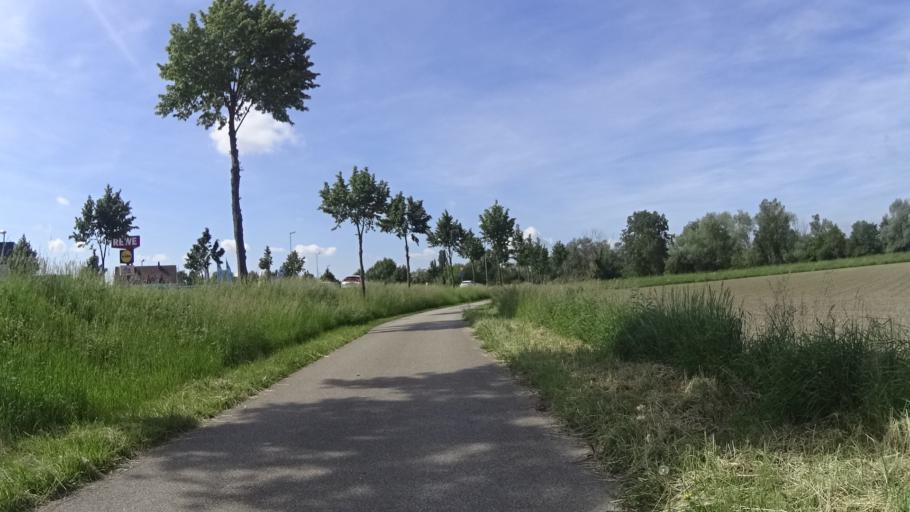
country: DE
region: Baden-Wuerttemberg
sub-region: Freiburg Region
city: Kehl
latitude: 48.5145
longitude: 7.8197
